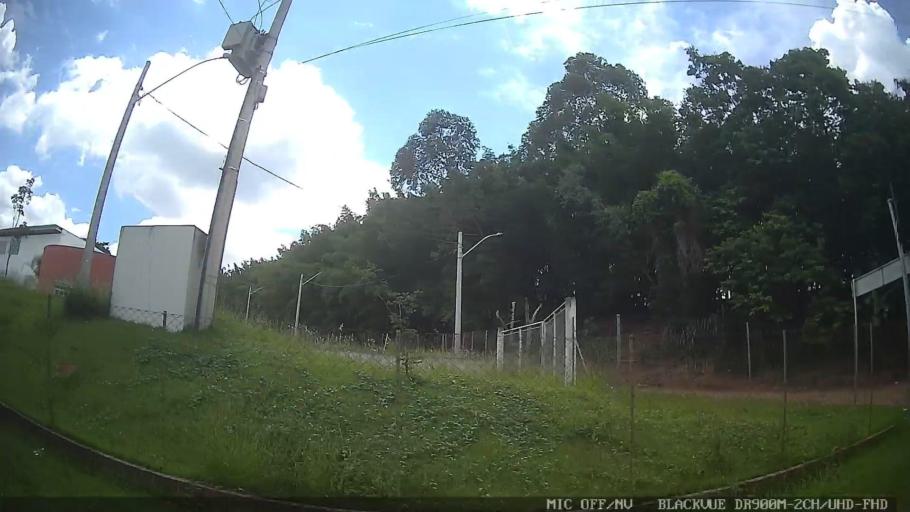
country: BR
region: Sao Paulo
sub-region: Jarinu
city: Jarinu
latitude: -23.0789
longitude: -46.6419
